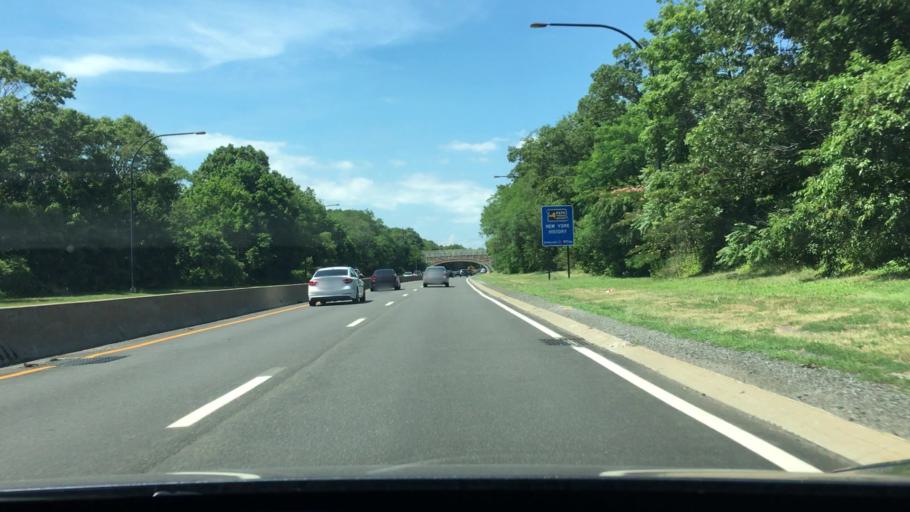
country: US
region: New York
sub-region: Nassau County
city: North Bellmore
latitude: 40.7052
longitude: -73.5243
